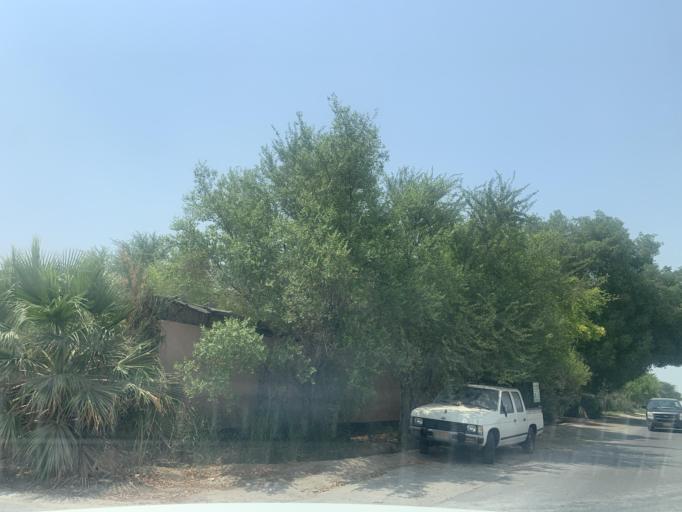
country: BH
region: Central Governorate
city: Madinat Hamad
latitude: 26.1220
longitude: 50.4731
